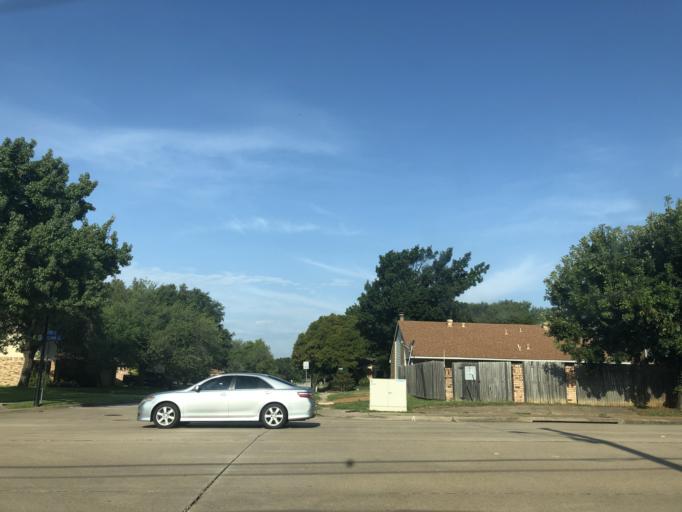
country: US
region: Texas
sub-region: Tarrant County
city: Euless
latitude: 32.8740
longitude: -97.0828
